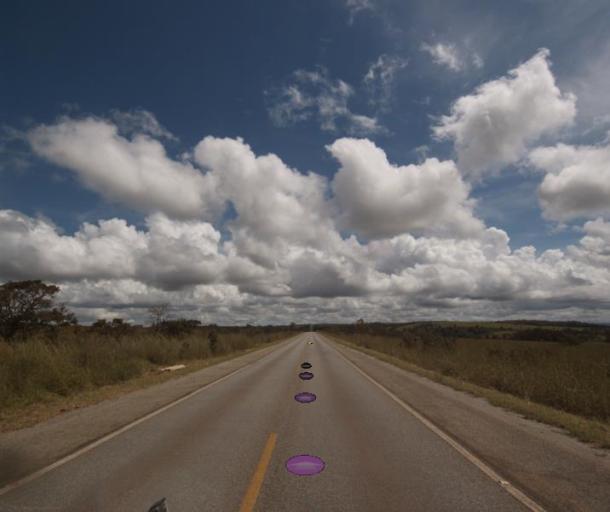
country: BR
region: Goias
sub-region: Pirenopolis
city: Pirenopolis
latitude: -15.7506
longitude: -48.6151
